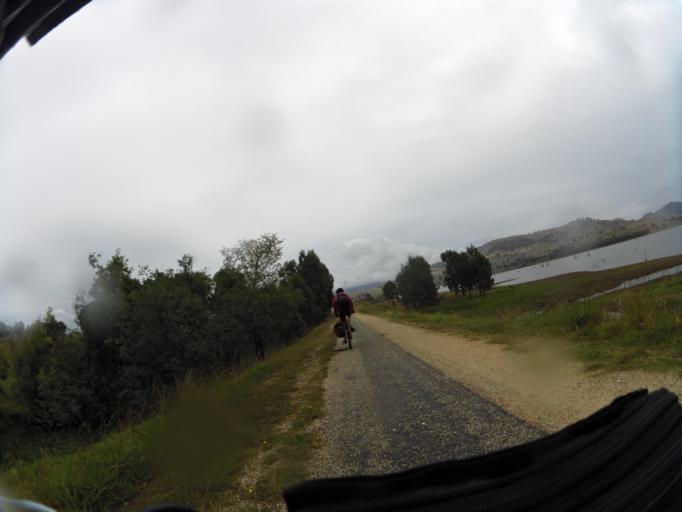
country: AU
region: New South Wales
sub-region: Albury Municipality
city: East Albury
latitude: -36.2341
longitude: 147.0953
